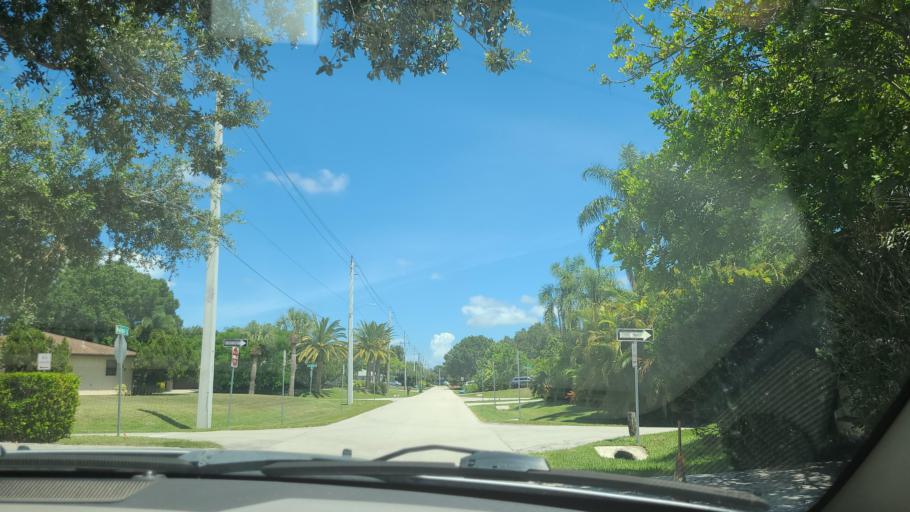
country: US
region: Florida
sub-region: Indian River County
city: Sebastian
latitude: 27.7879
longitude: -80.4888
